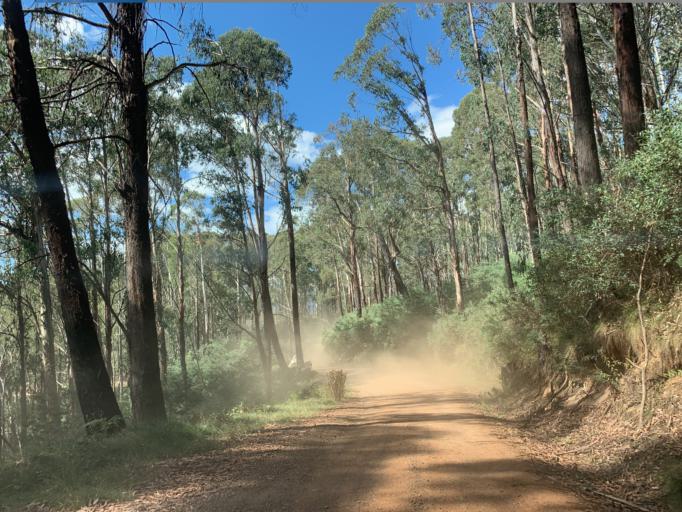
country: AU
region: Victoria
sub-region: Mansfield
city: Mansfield
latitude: -37.0956
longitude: 146.5399
